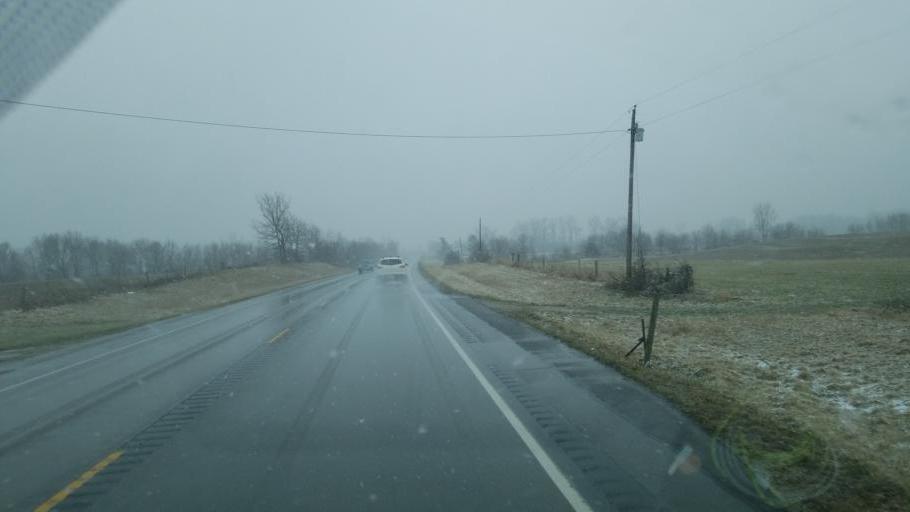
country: US
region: Indiana
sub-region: Grant County
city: Sweetser
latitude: 40.6475
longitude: -85.7098
